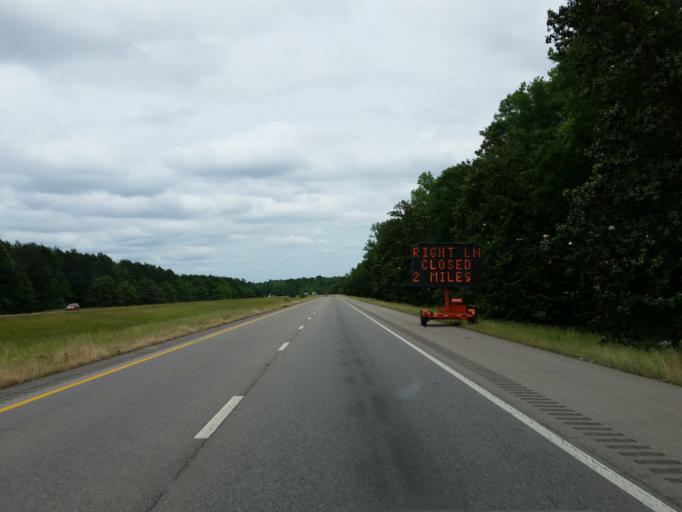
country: US
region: Mississippi
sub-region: Lauderdale County
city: Marion
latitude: 32.4118
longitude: -88.4856
